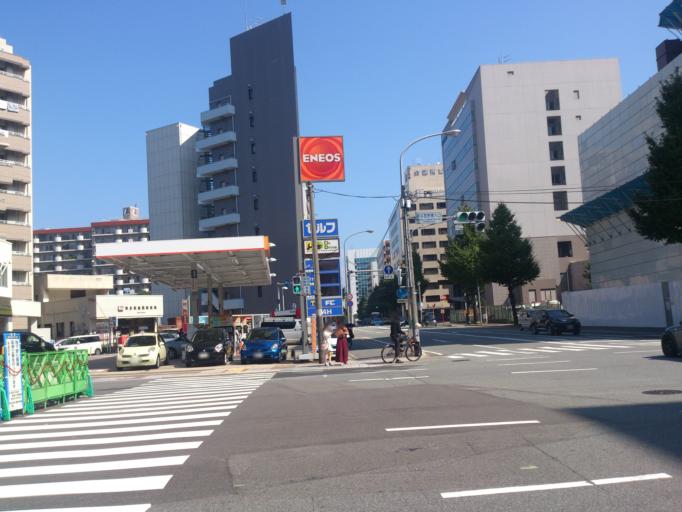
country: JP
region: Fukuoka
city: Fukuoka-shi
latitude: 33.5904
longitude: 130.4129
